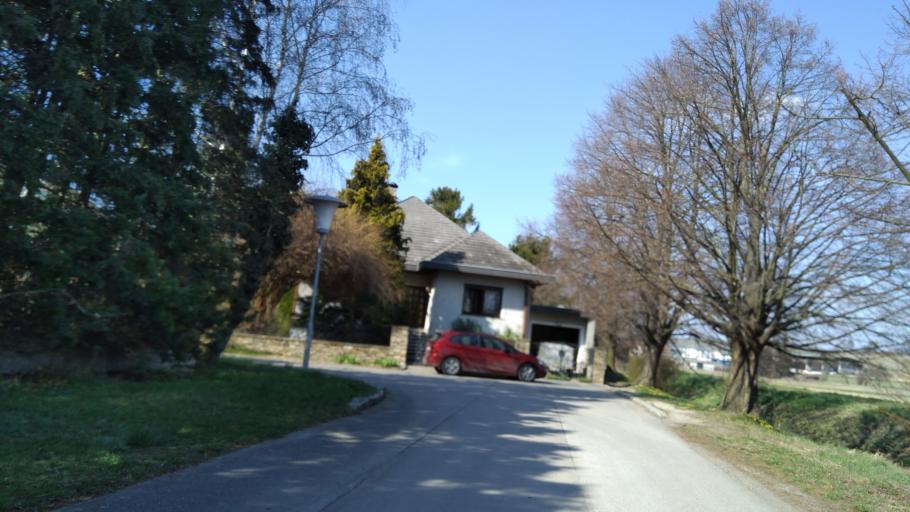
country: AT
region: Lower Austria
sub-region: Politischer Bezirk Mistelbach
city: Wolkersdorf im Weinviertel
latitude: 48.3756
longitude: 16.5267
